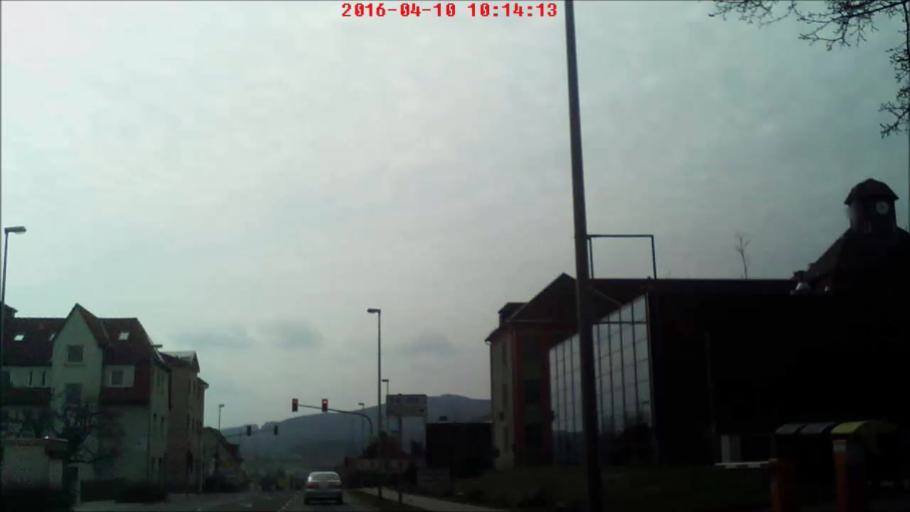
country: DE
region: Thuringia
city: Ilmenau
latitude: 50.6894
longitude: 10.9201
